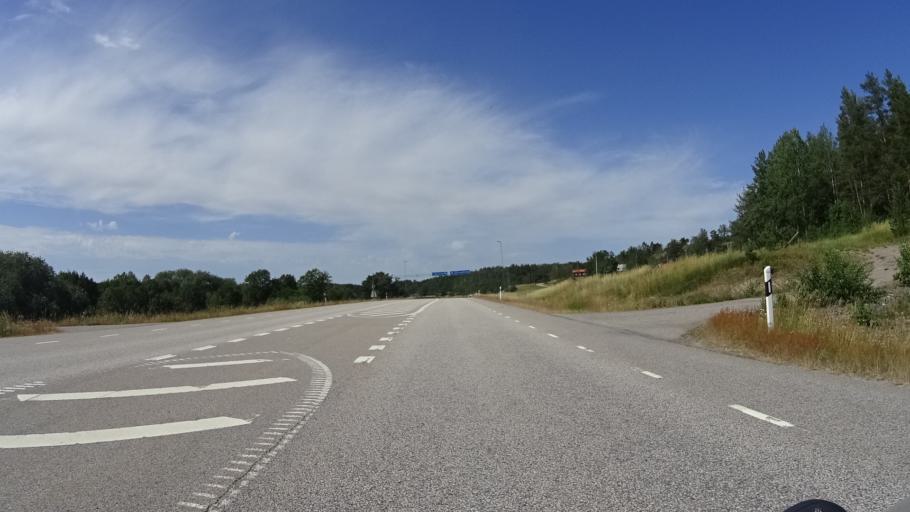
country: SE
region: Kalmar
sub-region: Vasterviks Kommun
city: Gamleby
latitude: 57.9132
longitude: 16.3782
